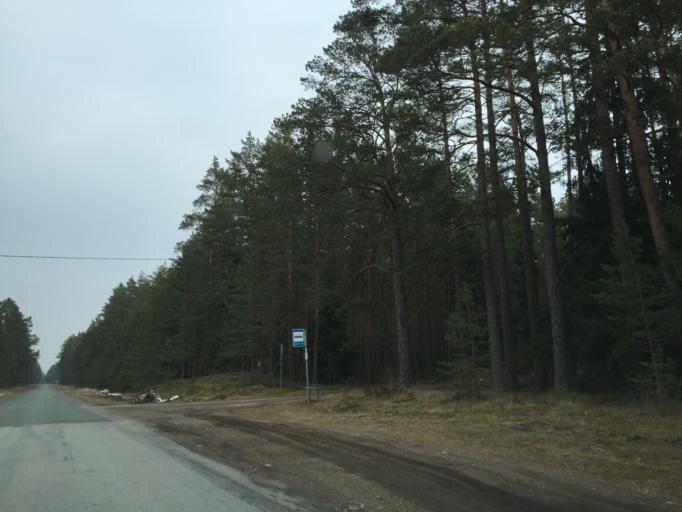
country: LV
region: Salacgrivas
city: Ainazi
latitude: 57.9868
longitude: 24.4223
